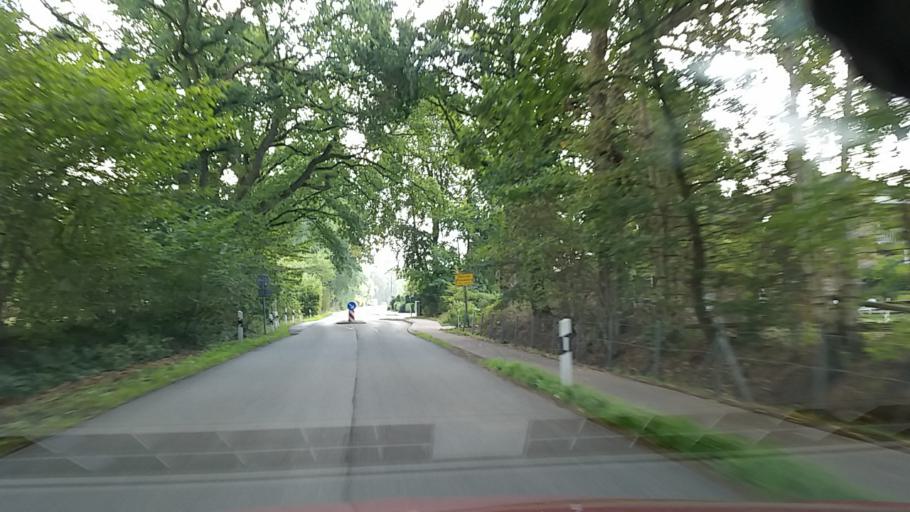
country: DE
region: Schleswig-Holstein
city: Rellingen
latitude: 53.6269
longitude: 9.7830
